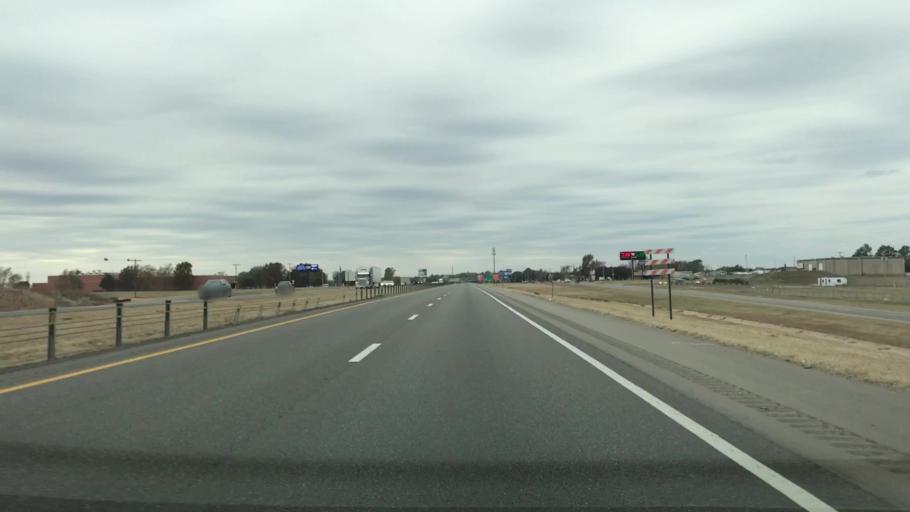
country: US
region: Oklahoma
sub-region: Custer County
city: Weatherford
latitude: 35.5364
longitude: -98.6667
